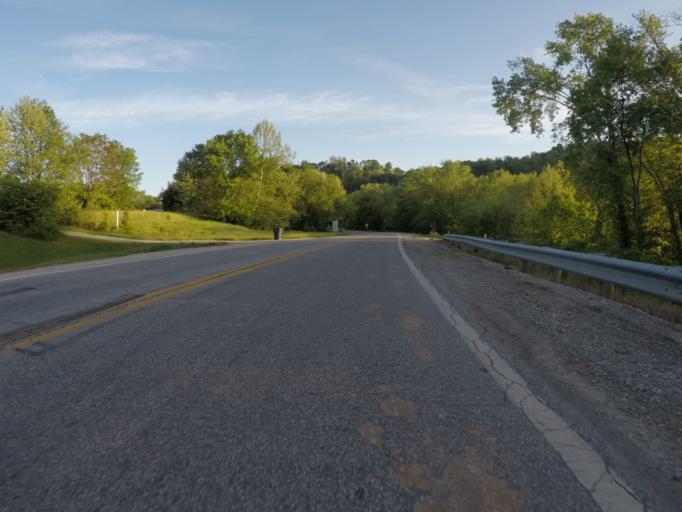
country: US
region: West Virginia
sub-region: Cabell County
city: Huntington
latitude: 38.4938
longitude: -82.4768
